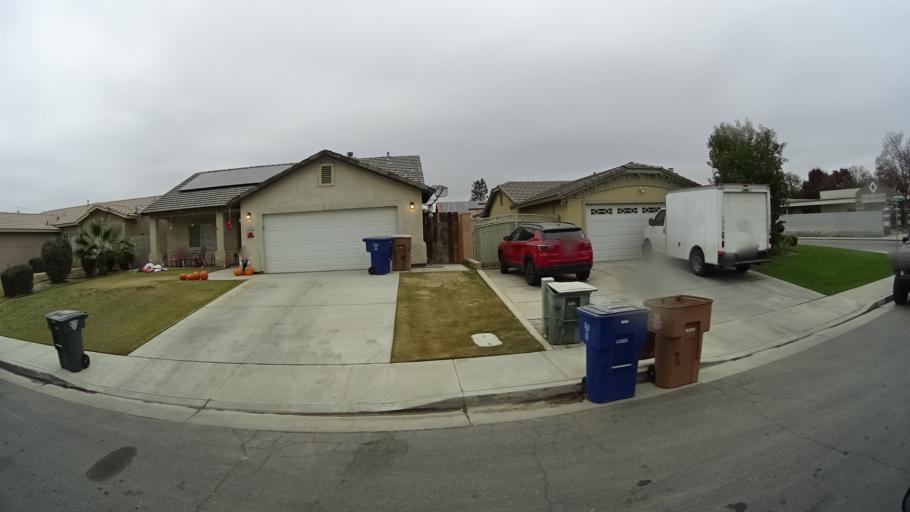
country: US
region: California
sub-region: Kern County
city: Greenfield
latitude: 35.2892
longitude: -119.0466
